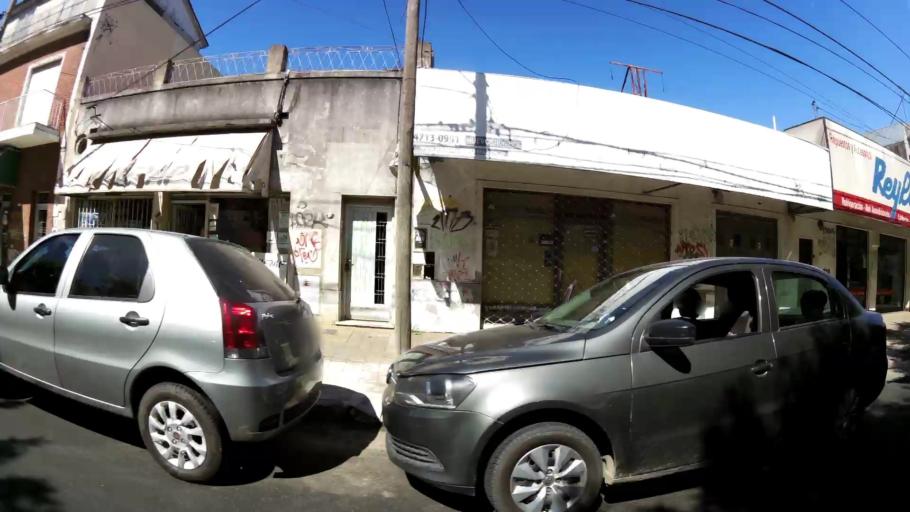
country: AR
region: Buenos Aires
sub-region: Partido de General San Martin
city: General San Martin
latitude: -34.5675
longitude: -58.5426
